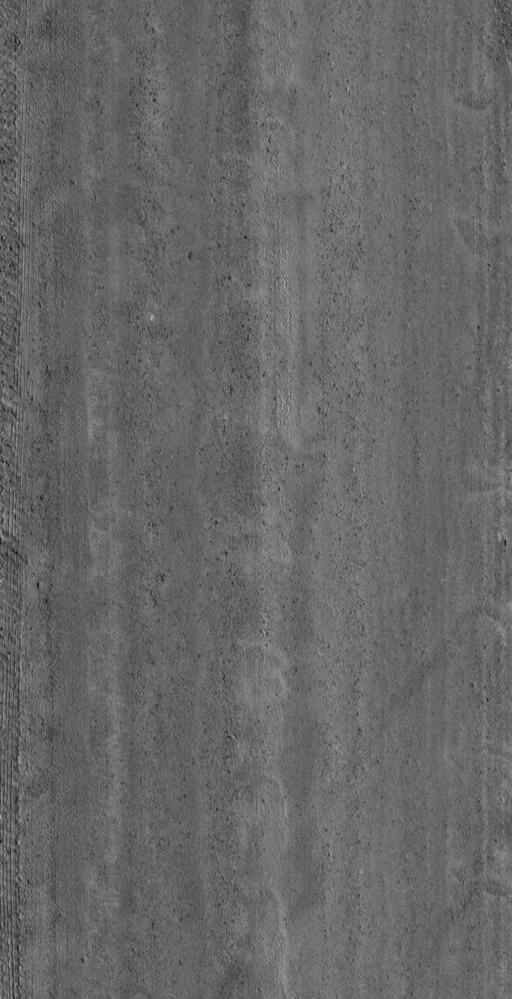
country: US
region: Vermont
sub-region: Washington County
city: Montpelier
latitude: 44.2584
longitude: -72.6142
